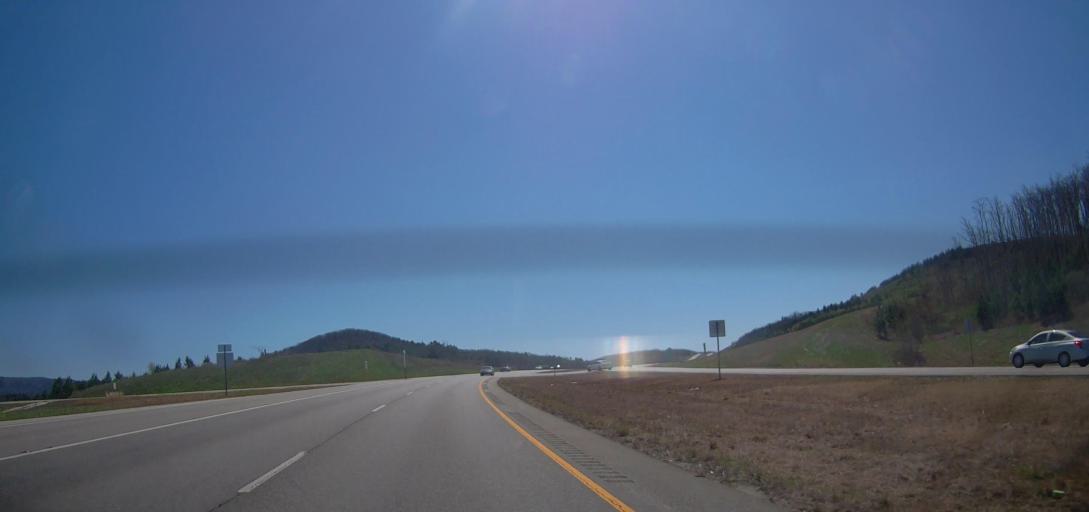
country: US
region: Alabama
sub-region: Calhoun County
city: Saks
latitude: 33.7007
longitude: -85.8092
